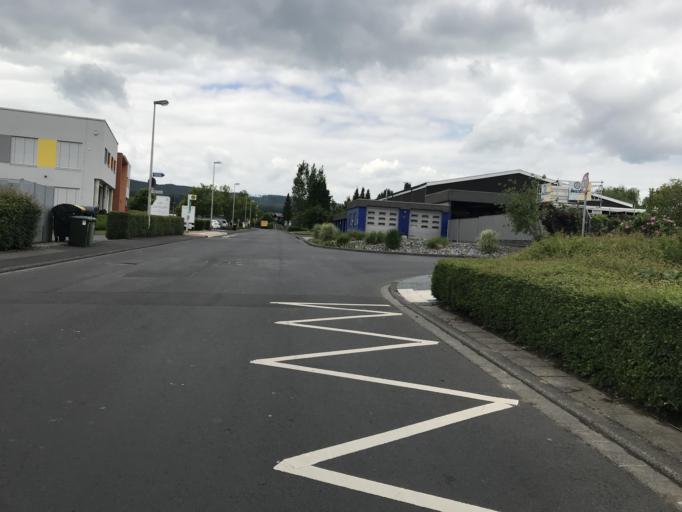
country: DE
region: Hesse
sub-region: Regierungsbezirk Kassel
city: Baunatal
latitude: 51.2534
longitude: 9.3905
